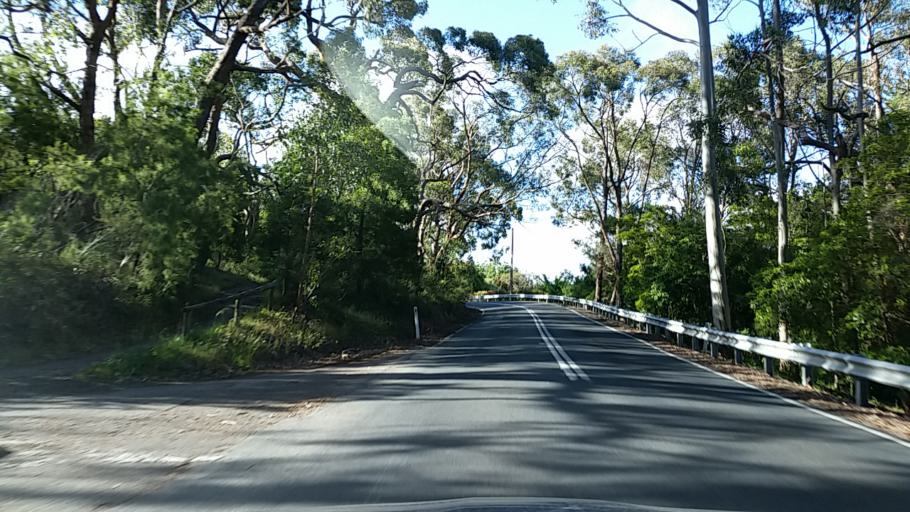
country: AU
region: South Australia
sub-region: Adelaide Hills
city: Stirling
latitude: -35.0221
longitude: 138.7542
